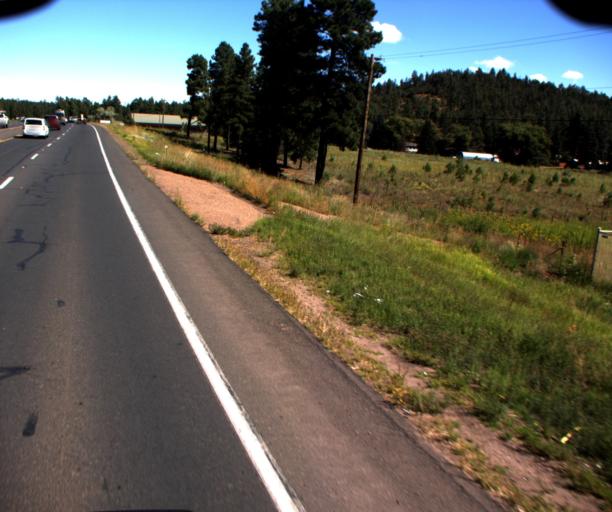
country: US
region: Arizona
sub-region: Navajo County
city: Show Low
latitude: 34.2162
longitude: -110.0287
